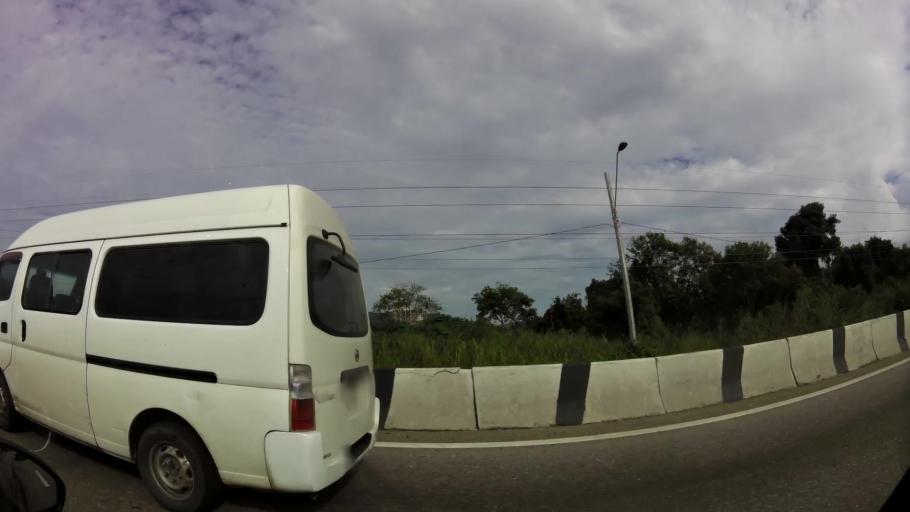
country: TT
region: City of Port of Spain
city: Mucurapo
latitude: 10.6663
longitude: -61.5363
